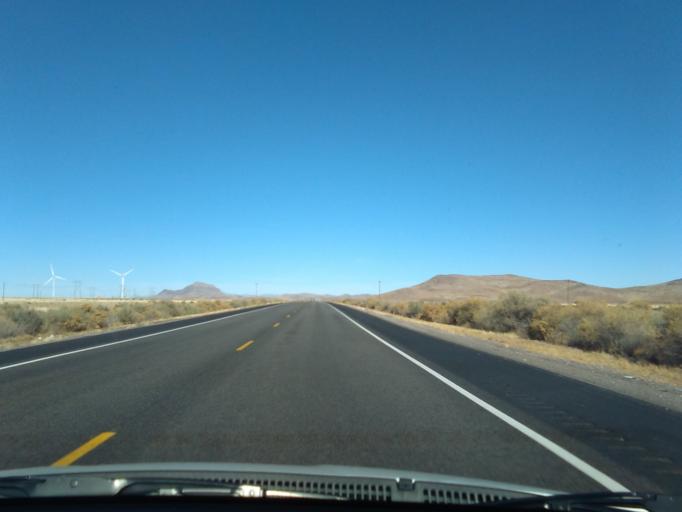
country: US
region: New Mexico
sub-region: Luna County
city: Deming
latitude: 32.5153
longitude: -107.5013
